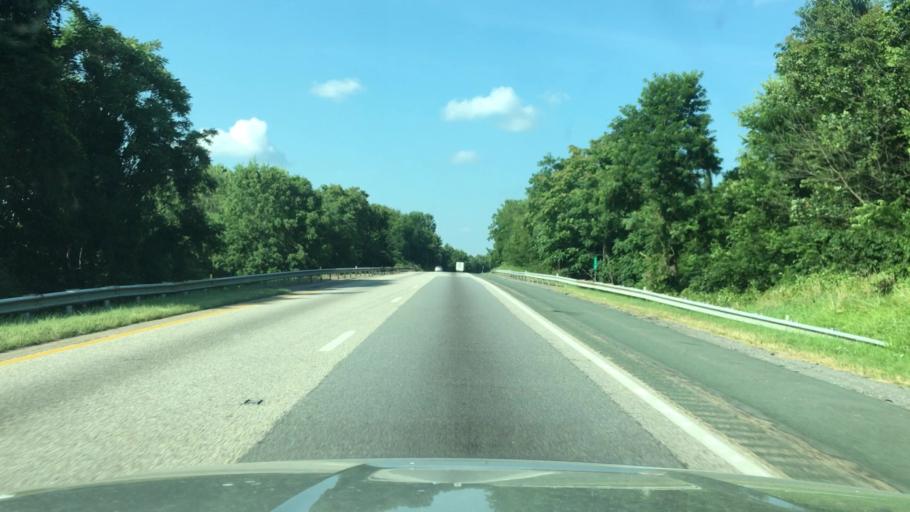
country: US
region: Virginia
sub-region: Rockbridge County
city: Glasgow
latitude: 37.6465
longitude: -79.5556
